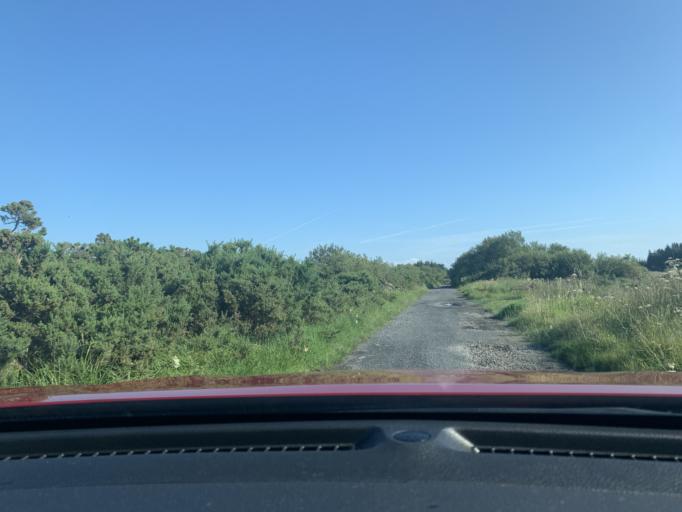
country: IE
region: Connaught
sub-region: Sligo
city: Tobercurry
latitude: 54.0656
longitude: -8.7926
